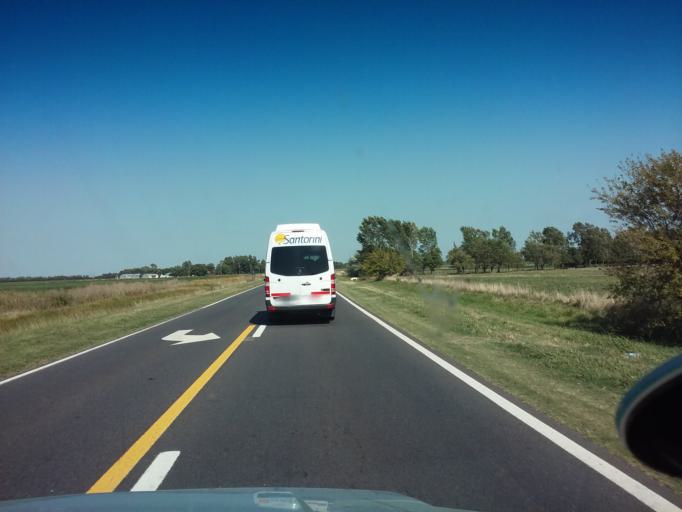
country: AR
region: Buenos Aires
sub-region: Partido de Chivilcoy
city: Chivilcoy
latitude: -34.9563
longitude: -60.0269
